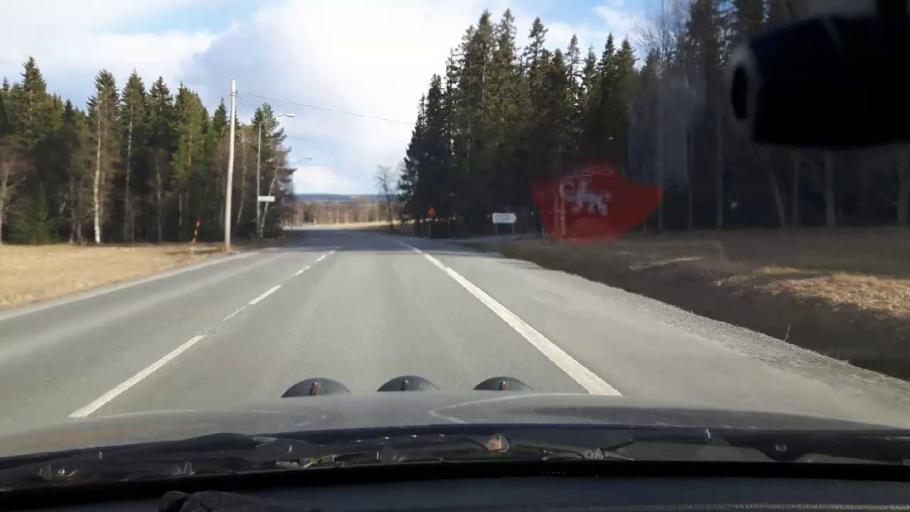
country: SE
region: Jaemtland
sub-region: OEstersunds Kommun
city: Ostersund
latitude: 63.1746
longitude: 14.5330
